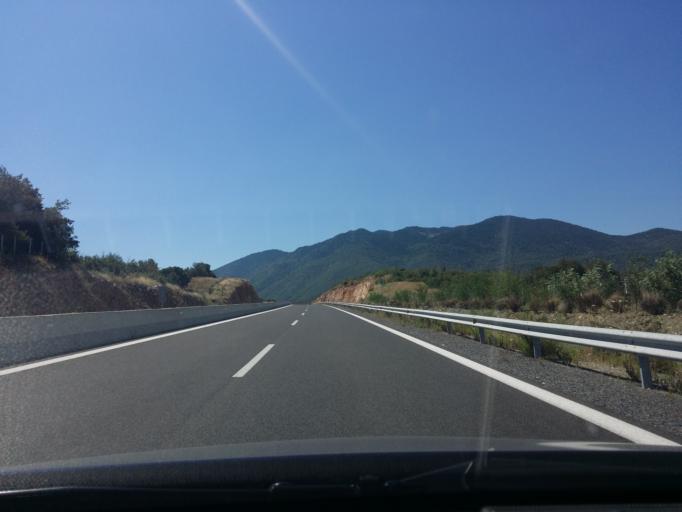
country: GR
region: Peloponnese
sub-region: Nomos Arkadias
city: Megalopoli
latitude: 37.2934
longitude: 22.2119
